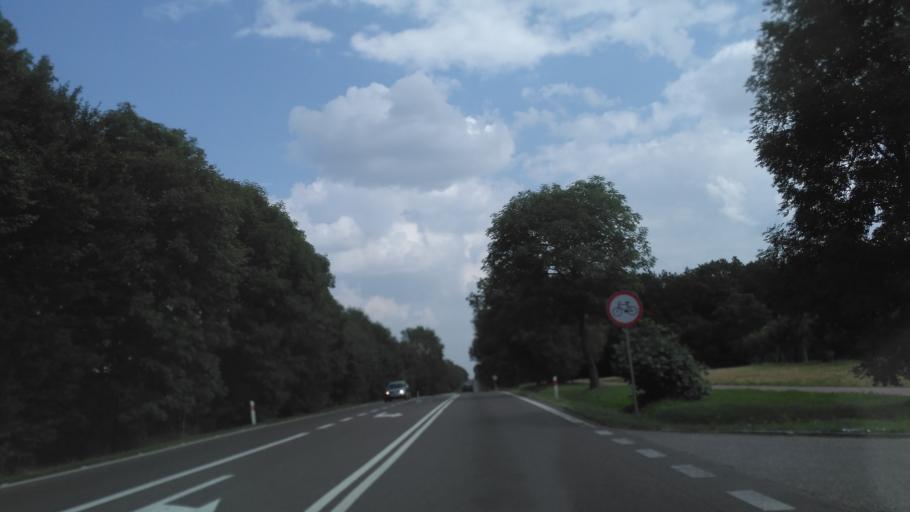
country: PL
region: Lublin Voivodeship
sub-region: Chelm
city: Chelm
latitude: 51.1589
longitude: 23.3993
